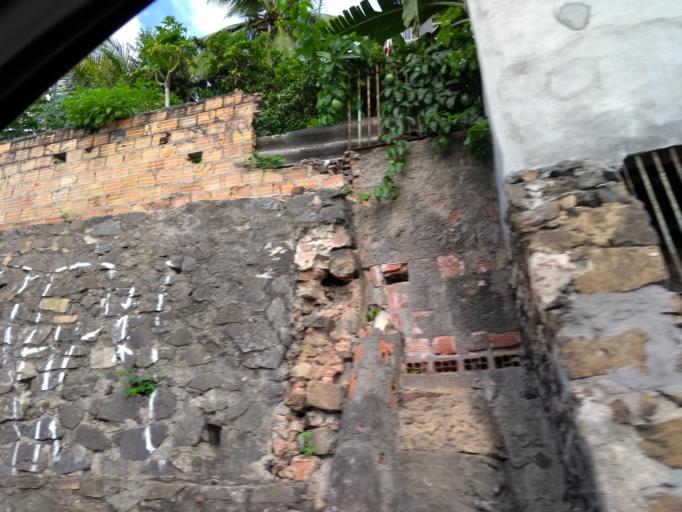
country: BR
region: Bahia
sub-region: Salvador
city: Salvador
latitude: -12.9831
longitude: -38.5202
